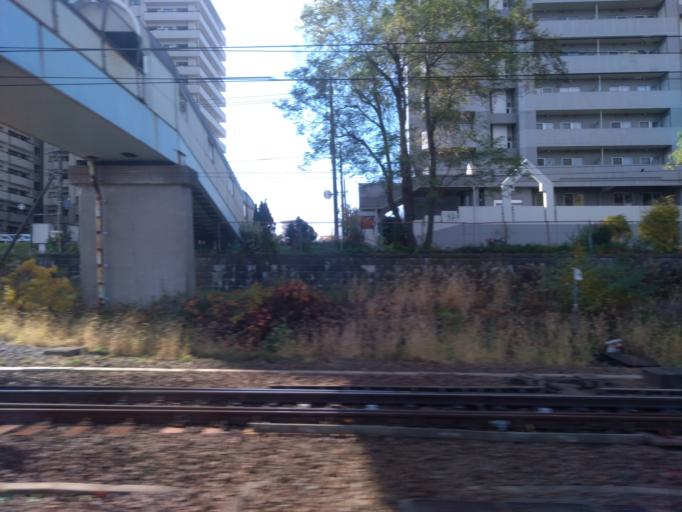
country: JP
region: Hokkaido
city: Kitahiroshima
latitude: 42.9820
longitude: 141.5629
